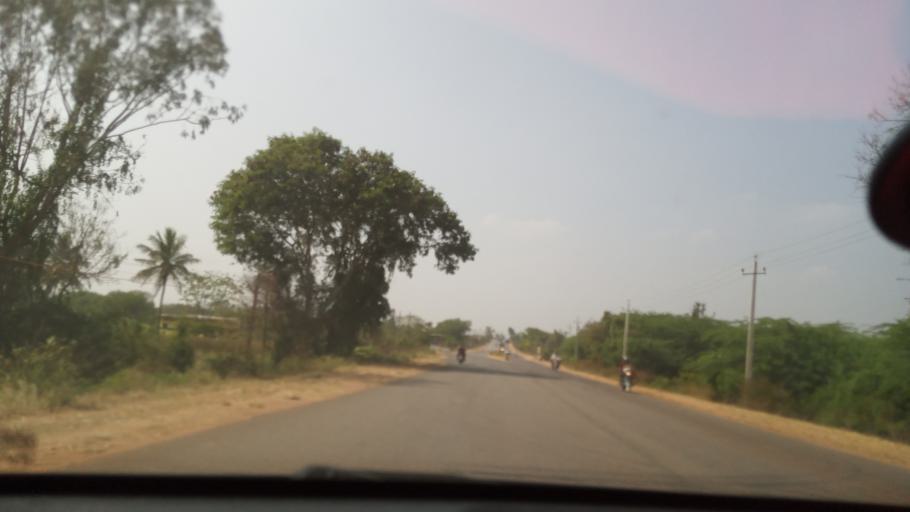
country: IN
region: Karnataka
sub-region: Mysore
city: Nanjangud
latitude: 12.0894
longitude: 76.7270
